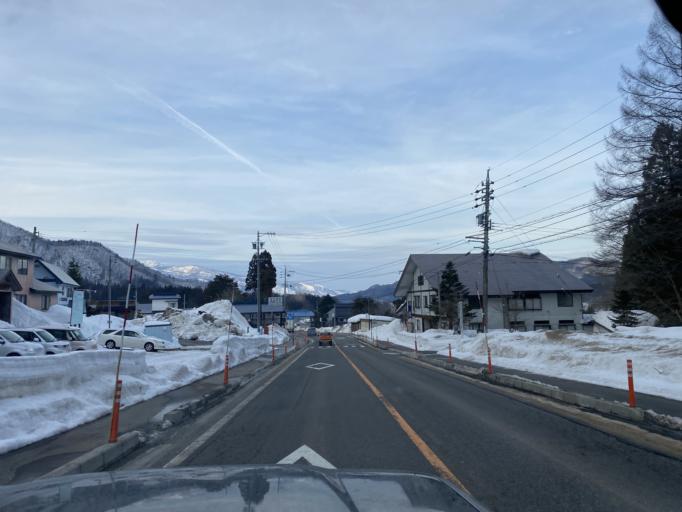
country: JP
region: Nagano
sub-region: Kitaazumi Gun
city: Hakuba
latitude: 36.6300
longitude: 137.8445
